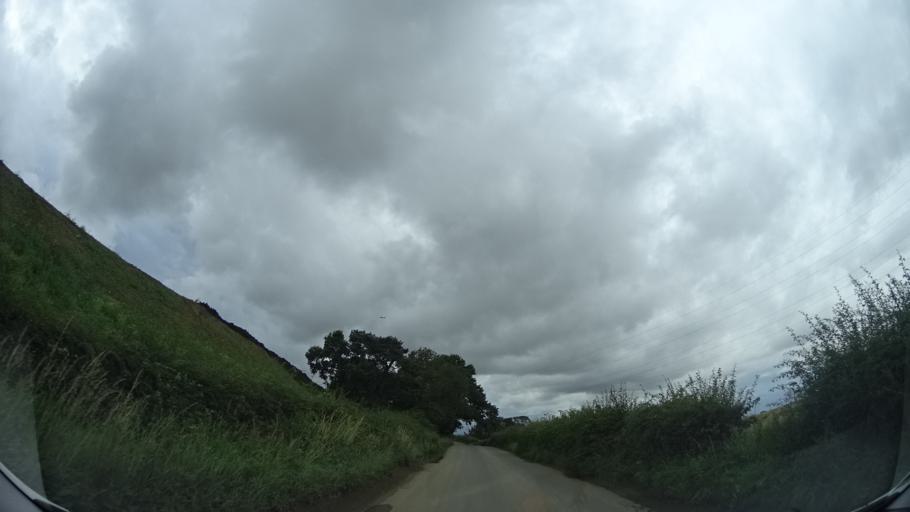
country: GB
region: Scotland
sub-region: West Lothian
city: Kirknewton
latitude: 55.9045
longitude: -3.4352
